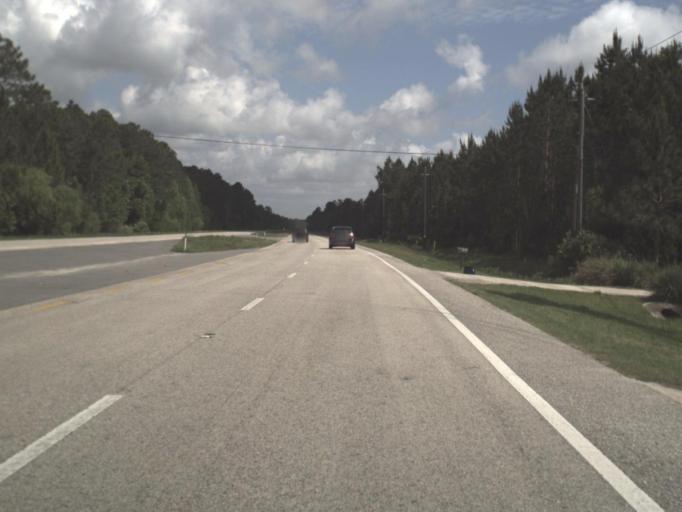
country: US
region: Florida
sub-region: Saint Johns County
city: Butler Beach
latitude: 29.7345
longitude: -81.3070
